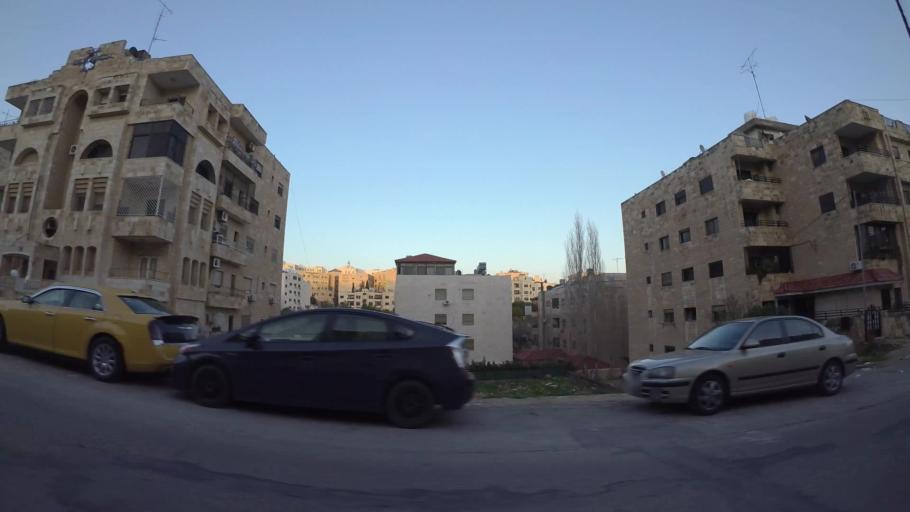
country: JO
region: Amman
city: Al Jubayhah
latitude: 31.9917
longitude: 35.8778
